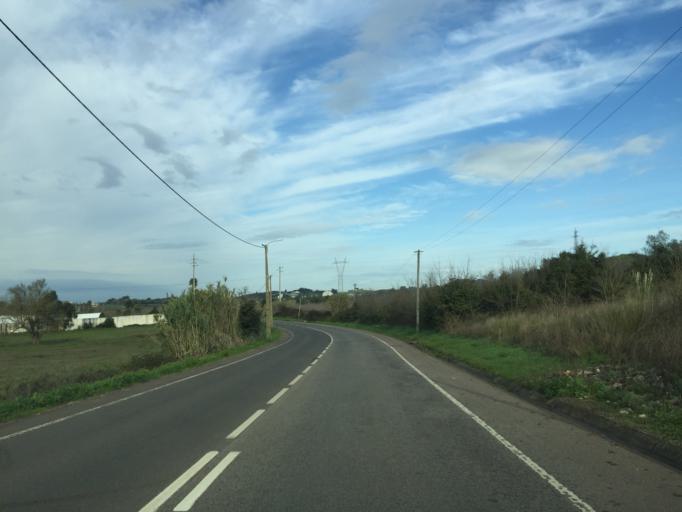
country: PT
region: Lisbon
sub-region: Sintra
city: Almargem
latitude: 38.8542
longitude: -9.2726
